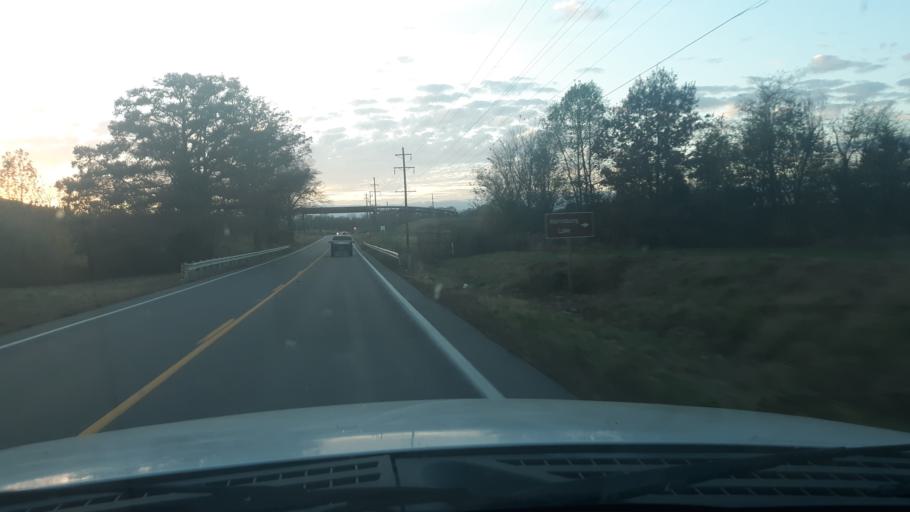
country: US
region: Illinois
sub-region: Saline County
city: Harrisburg
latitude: 37.8347
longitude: -88.5785
